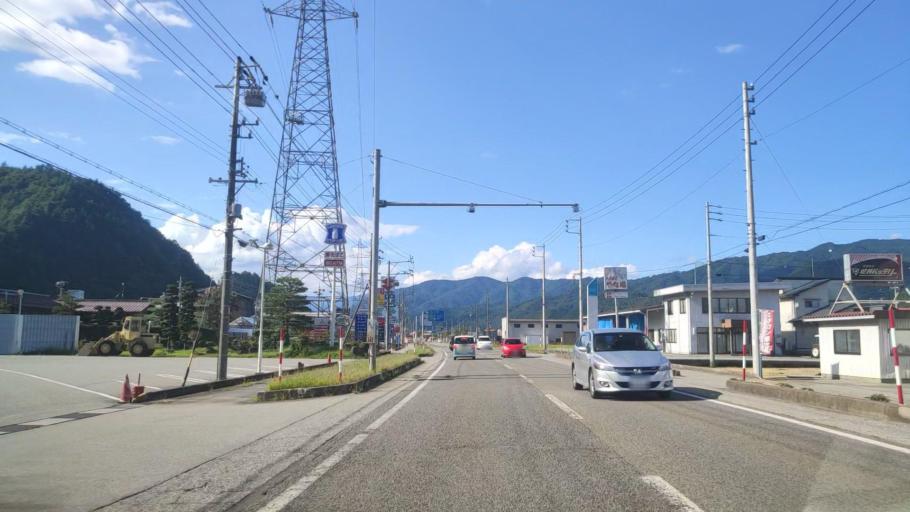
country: JP
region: Gifu
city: Takayama
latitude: 36.2324
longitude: 137.1798
